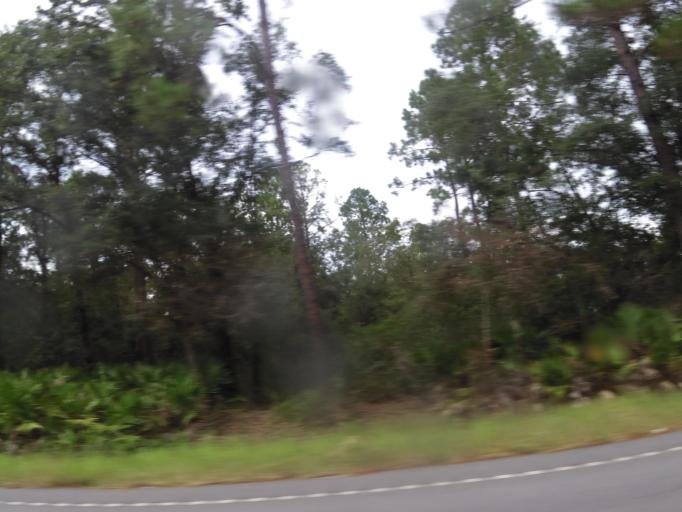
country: US
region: Florida
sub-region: Nassau County
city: Hilliard
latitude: 30.5218
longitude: -82.0447
